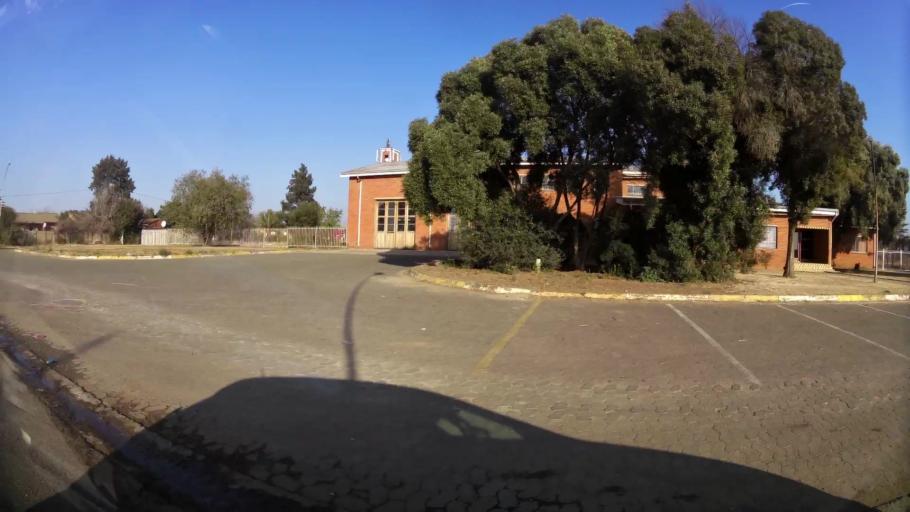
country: ZA
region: Orange Free State
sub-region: Mangaung Metropolitan Municipality
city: Bloemfontein
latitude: -29.1529
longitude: 26.2175
